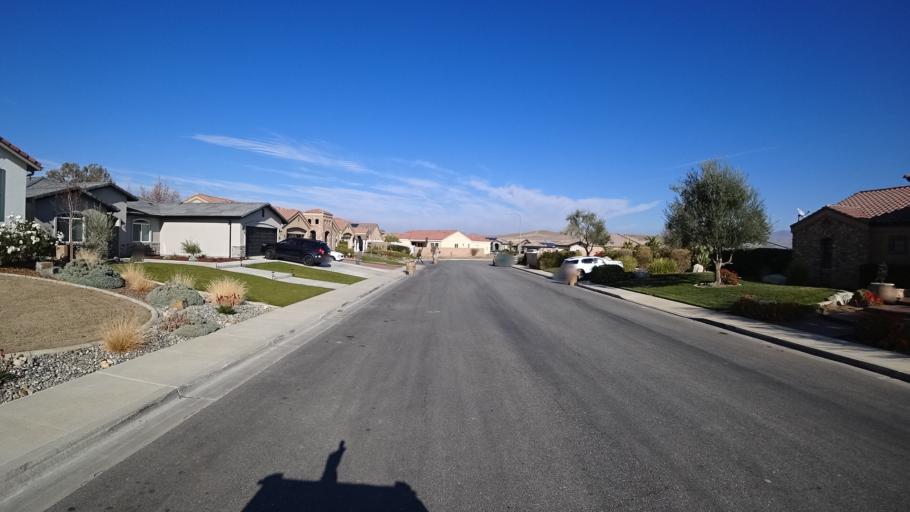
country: US
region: California
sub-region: Kern County
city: Oildale
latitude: 35.4144
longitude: -118.8913
